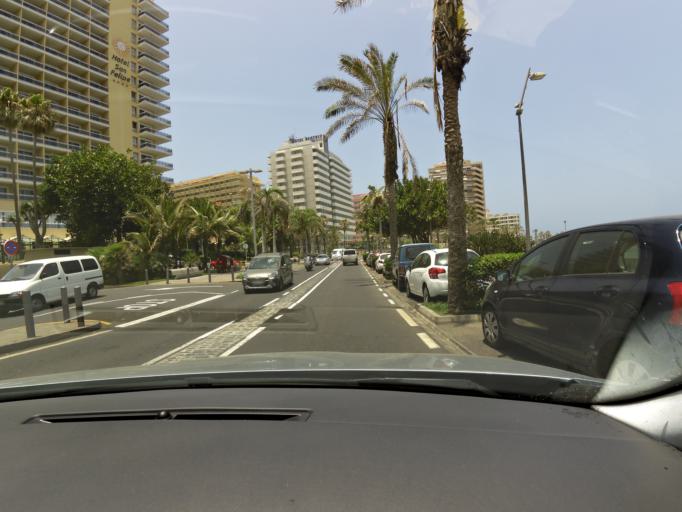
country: ES
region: Canary Islands
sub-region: Provincia de Santa Cruz de Tenerife
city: Puerto de la Cruz
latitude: 28.4166
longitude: -16.5406
